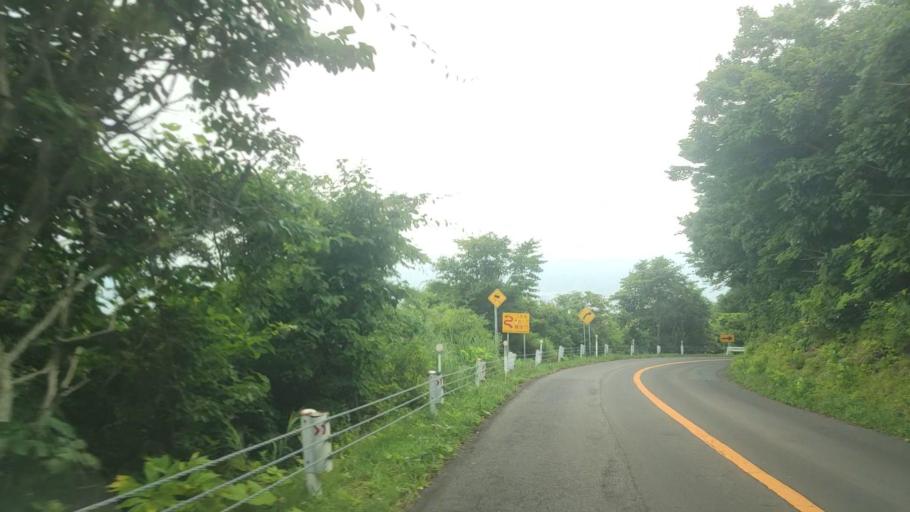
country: JP
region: Hokkaido
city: Hakodate
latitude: 41.7625
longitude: 140.6986
